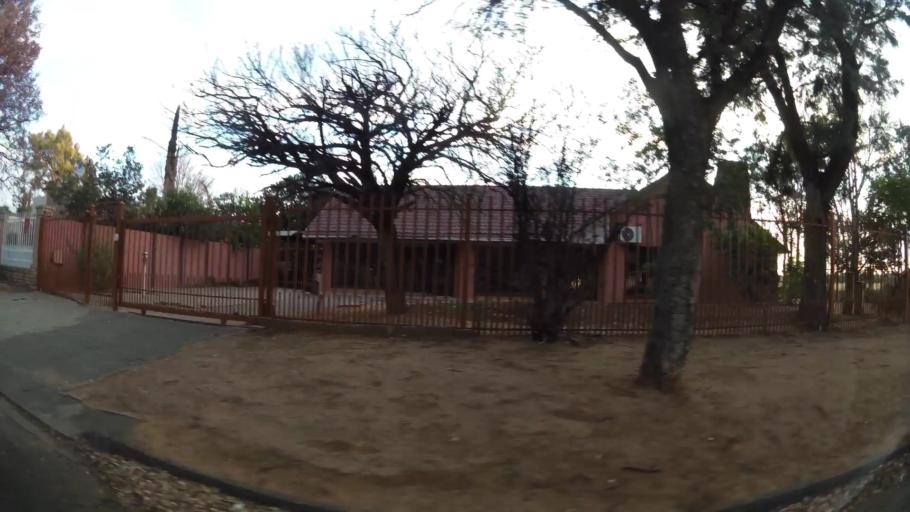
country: ZA
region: Orange Free State
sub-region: Mangaung Metropolitan Municipality
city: Bloemfontein
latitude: -29.1345
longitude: 26.1755
